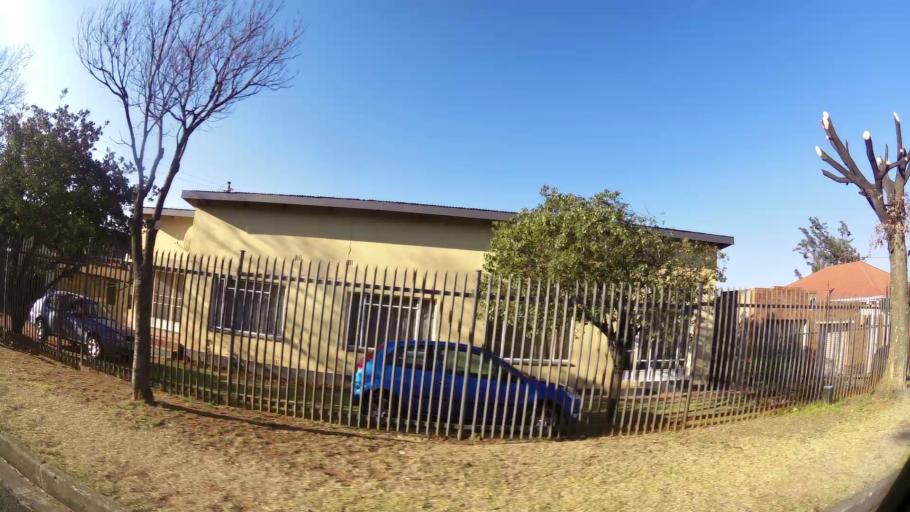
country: ZA
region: Gauteng
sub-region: Ekurhuleni Metropolitan Municipality
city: Germiston
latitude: -26.1888
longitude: 28.1486
